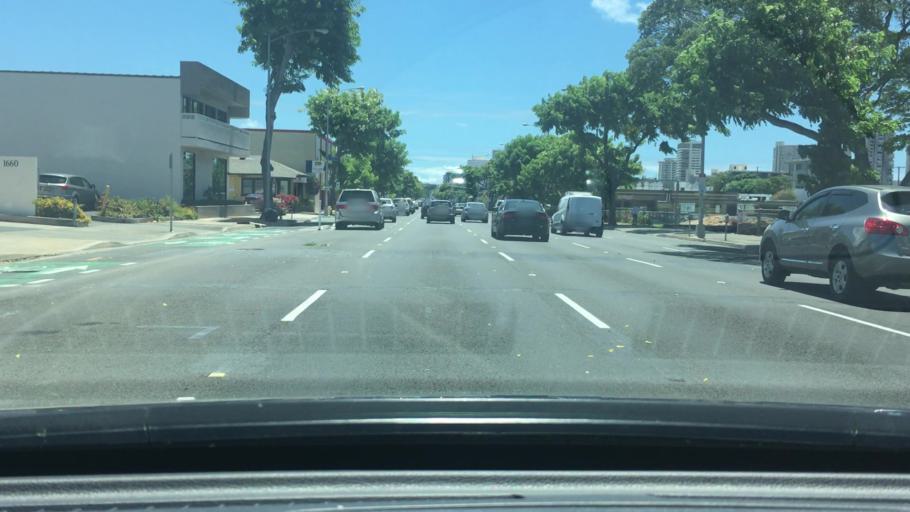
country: US
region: Hawaii
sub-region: Honolulu County
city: Honolulu
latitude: 21.2967
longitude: -157.8351
